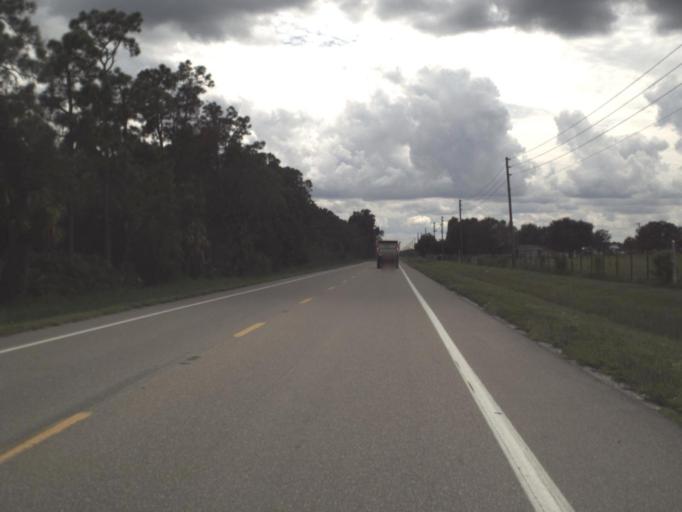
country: US
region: Florida
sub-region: DeSoto County
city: Nocatee
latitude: 27.0021
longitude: -81.7605
